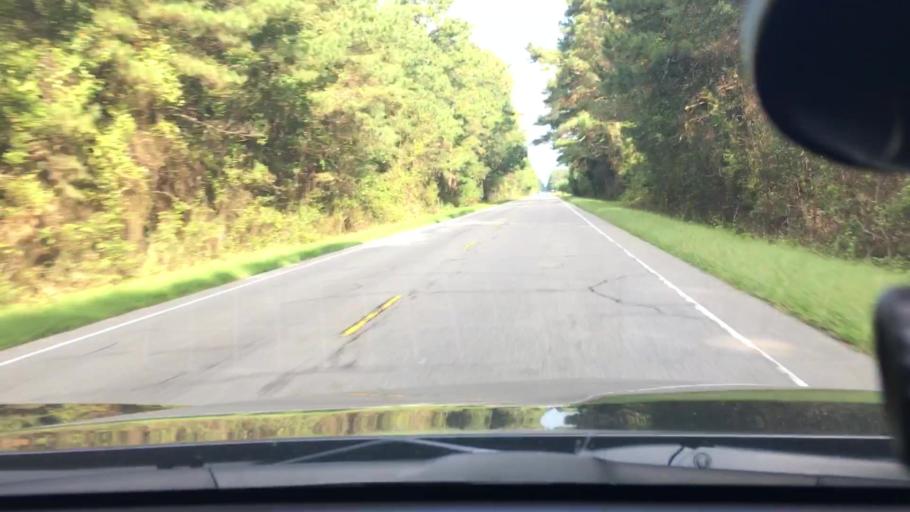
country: US
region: North Carolina
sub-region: Edgecombe County
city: Pinetops
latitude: 35.7571
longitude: -77.5518
